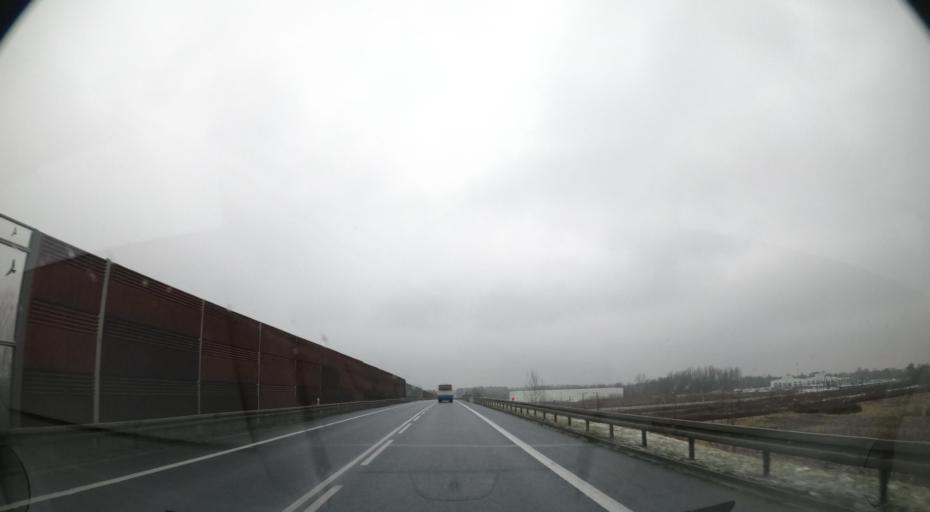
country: PL
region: Masovian Voivodeship
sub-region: Powiat sochaczewski
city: Sochaczew
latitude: 52.2190
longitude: 20.2576
